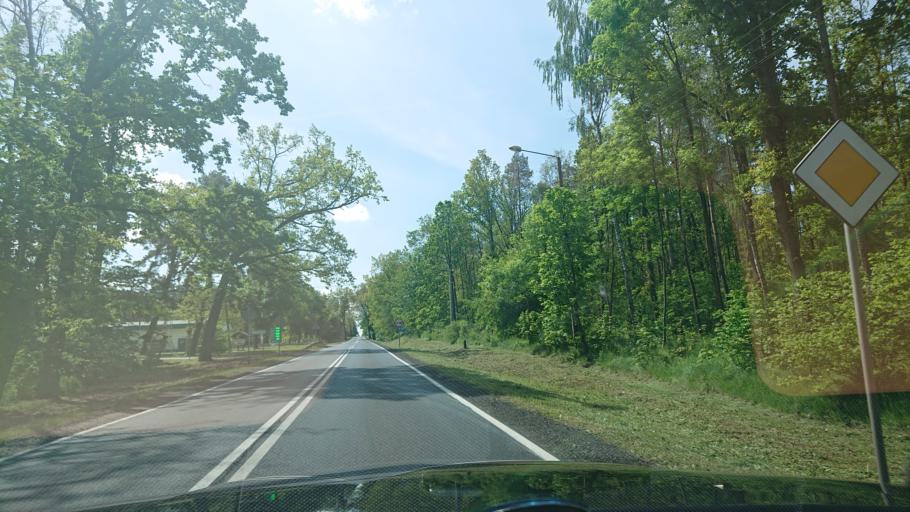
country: PL
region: Greater Poland Voivodeship
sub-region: Powiat gnieznienski
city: Gniezno
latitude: 52.4937
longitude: 17.5940
